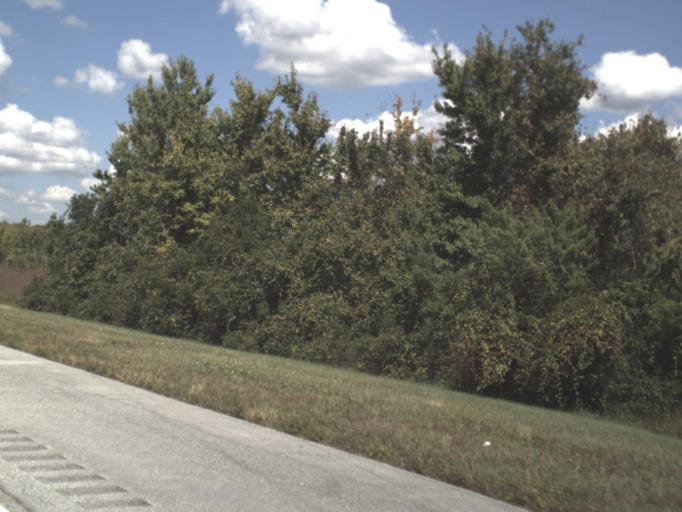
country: US
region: Florida
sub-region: Indian River County
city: Fellsmere
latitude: 27.7109
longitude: -80.8963
